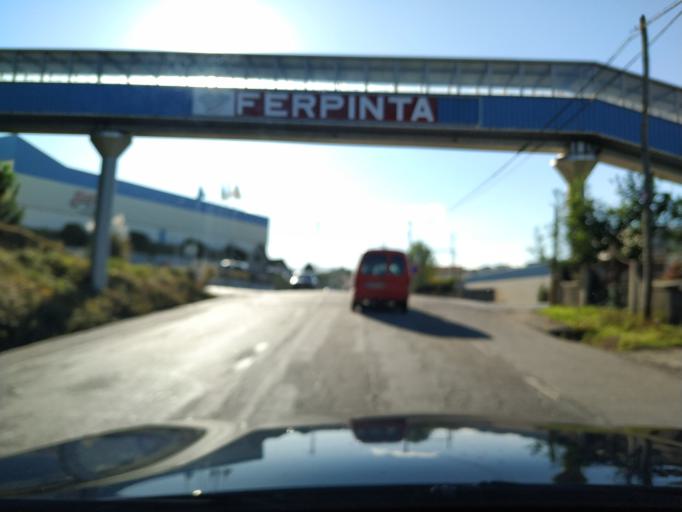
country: PT
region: Aveiro
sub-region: Vale de Cambra
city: Vale de Cambra
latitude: 40.8755
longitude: -8.4171
